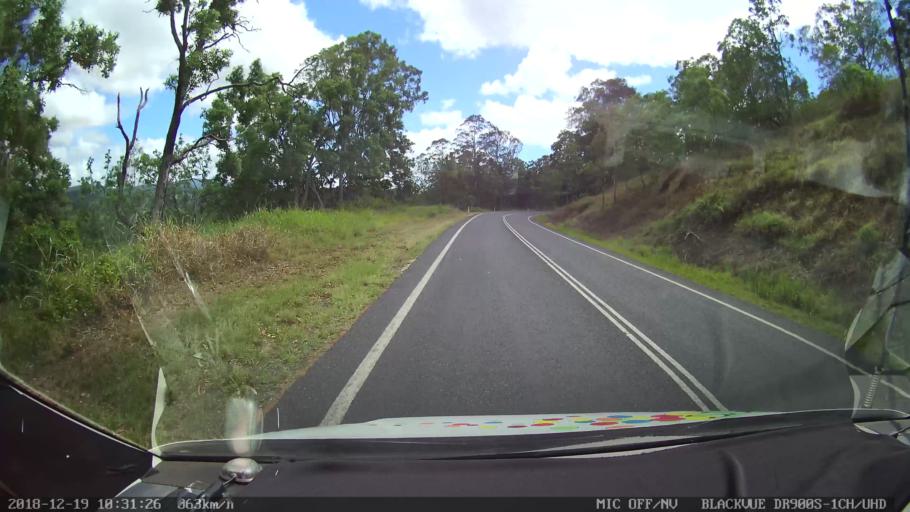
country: AU
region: New South Wales
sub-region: Lismore Municipality
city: Larnook
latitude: -28.5894
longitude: 153.1162
